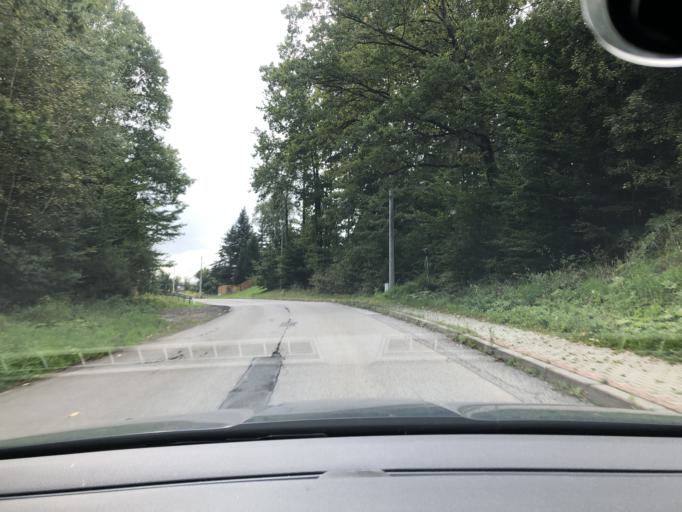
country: PL
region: Silesian Voivodeship
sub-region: Powiat zywiecki
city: Zarzecze
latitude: 49.7298
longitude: 19.1862
